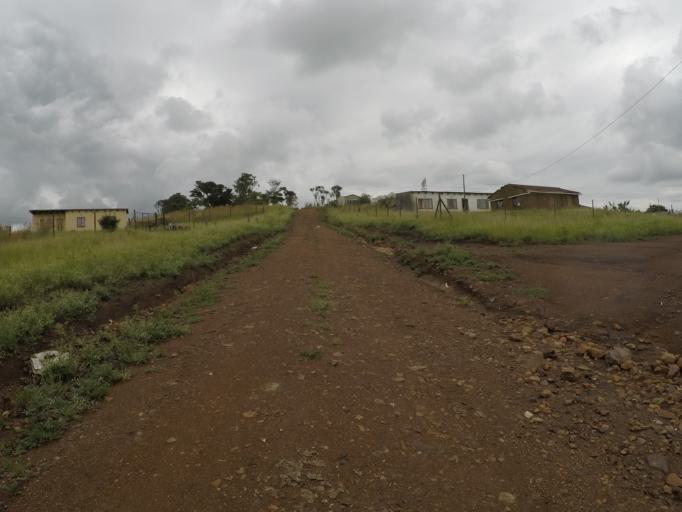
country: ZA
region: KwaZulu-Natal
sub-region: uThungulu District Municipality
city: Empangeni
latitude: -28.7105
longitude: 31.8522
